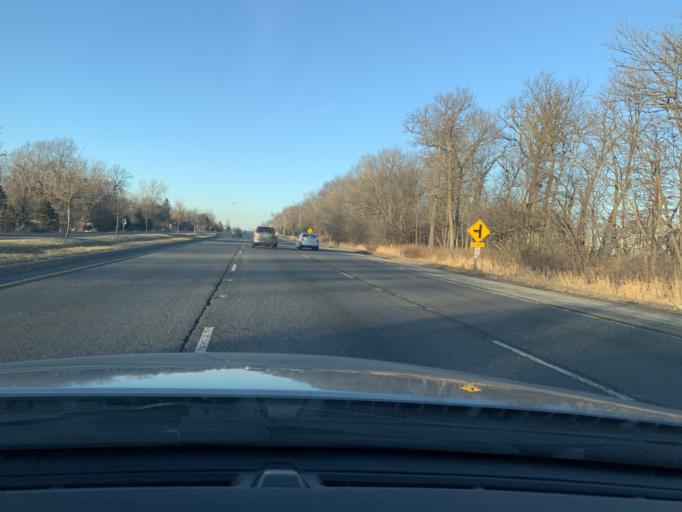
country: US
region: Illinois
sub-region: DuPage County
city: Bensenville
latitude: 41.9485
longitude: -87.9593
